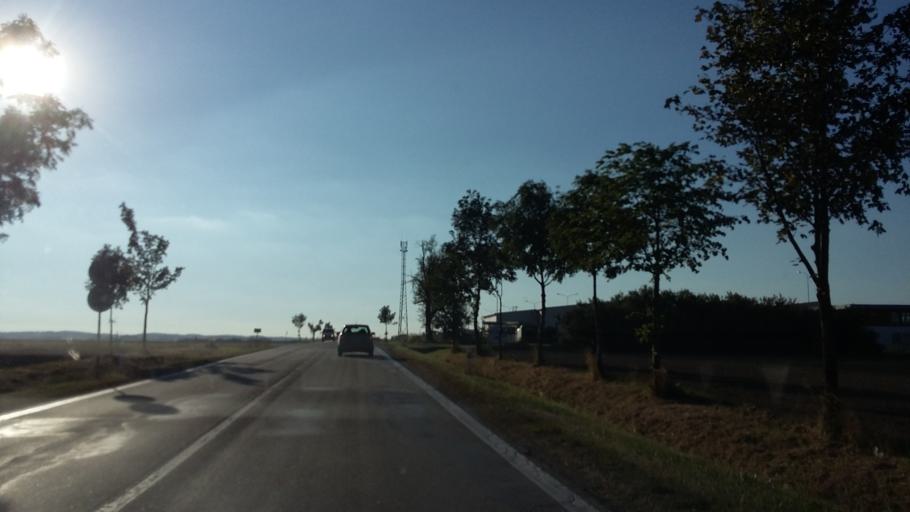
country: CZ
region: Vysocina
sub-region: Okres Zd'ar nad Sazavou
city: Velke Mezirici
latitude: 49.3757
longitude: 15.9485
